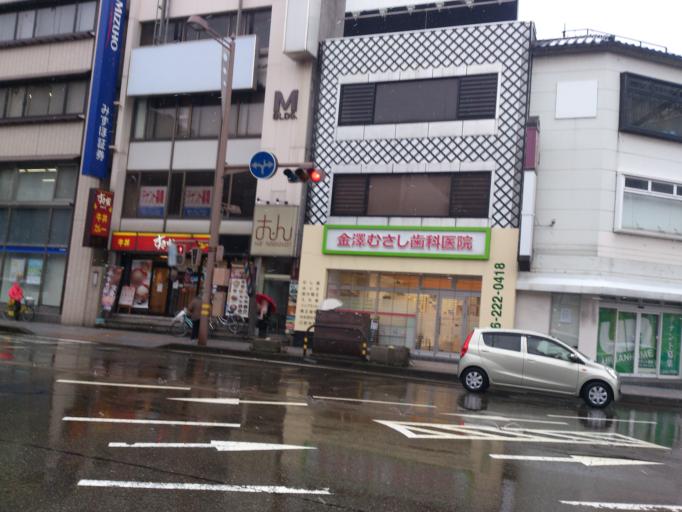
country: JP
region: Ishikawa
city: Kanazawa-shi
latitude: 36.5711
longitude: 136.6550
